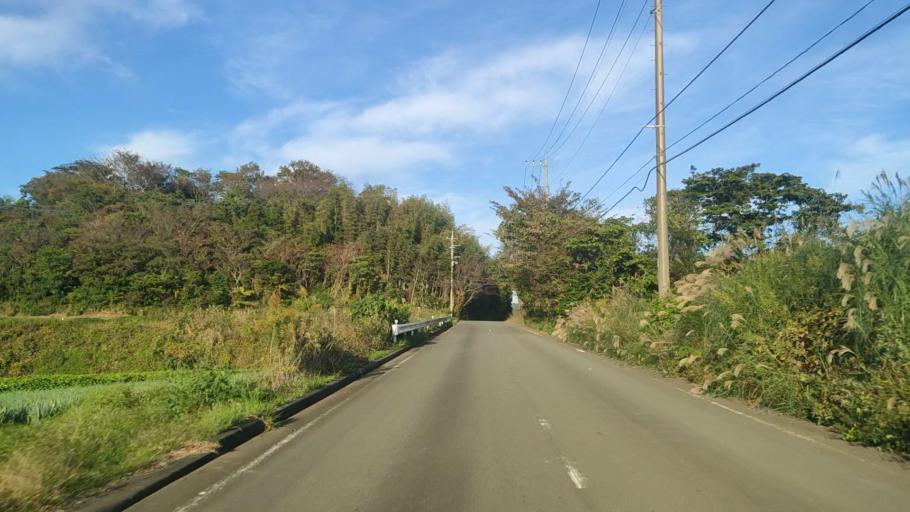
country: JP
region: Shizuoka
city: Mishima
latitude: 35.1415
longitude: 138.9507
